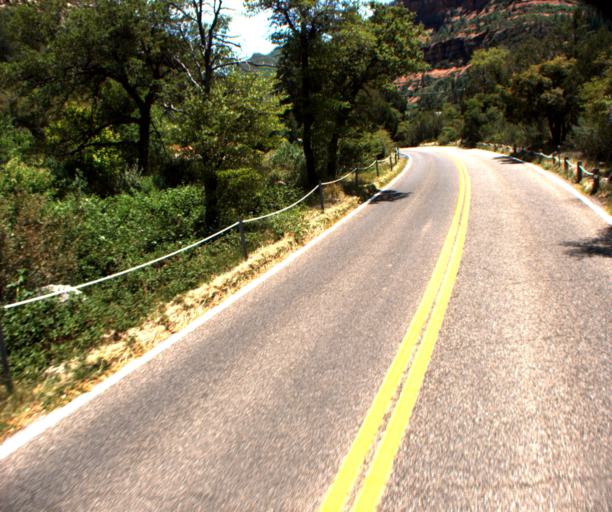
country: US
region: Arizona
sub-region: Coconino County
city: Sedona
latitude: 34.9488
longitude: -111.7539
